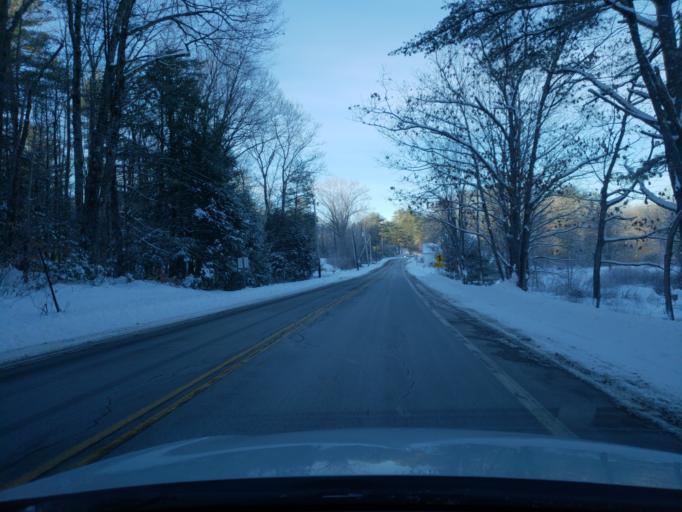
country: US
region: New Hampshire
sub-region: Hillsborough County
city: New Boston
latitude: 42.9818
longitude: -71.6803
